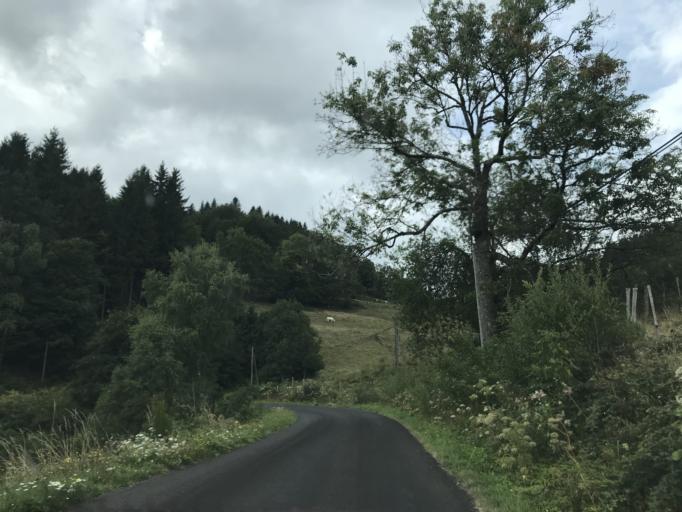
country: FR
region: Auvergne
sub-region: Departement du Puy-de-Dome
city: Job
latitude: 45.6736
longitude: 3.7497
